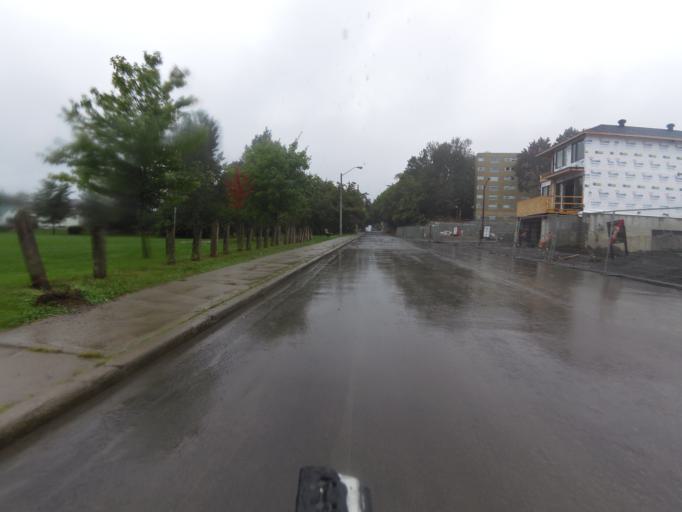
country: CA
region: Ontario
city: Ottawa
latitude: 45.4073
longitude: -75.6733
